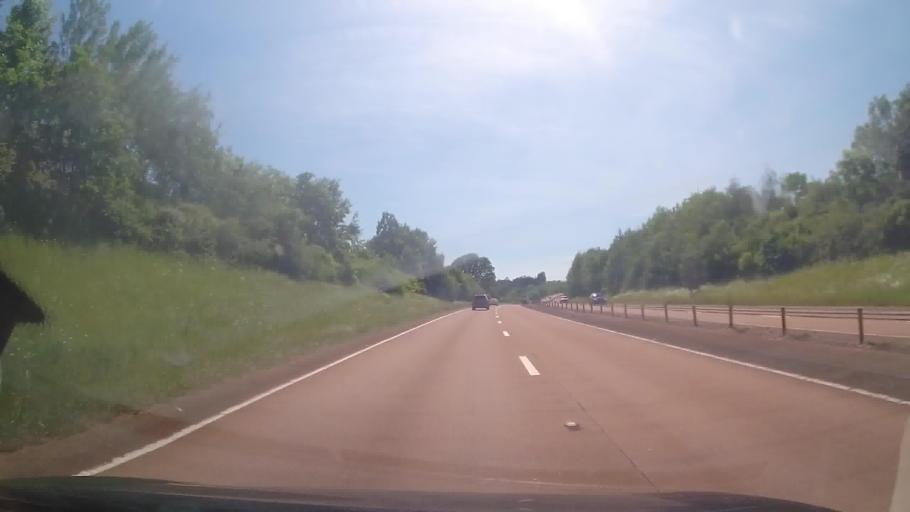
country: GB
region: England
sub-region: Devon
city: Newton Poppleford
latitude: 50.7365
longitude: -3.3686
